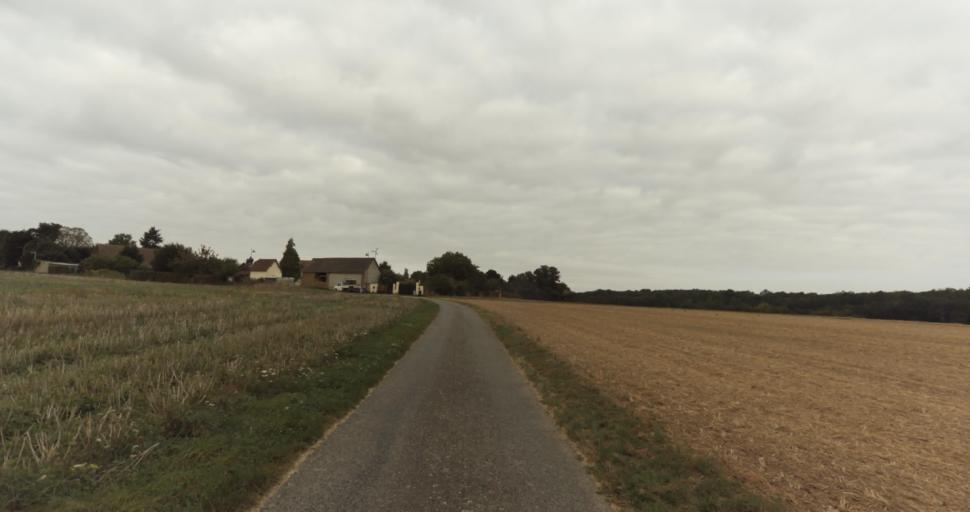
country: FR
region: Centre
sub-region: Departement d'Eure-et-Loir
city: Vert-en-Drouais
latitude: 48.8063
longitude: 1.2928
